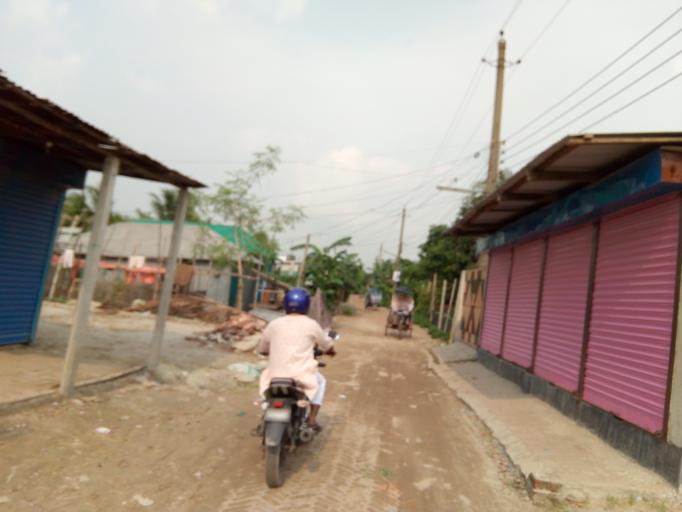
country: BD
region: Dhaka
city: Paltan
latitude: 23.7606
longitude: 90.4685
